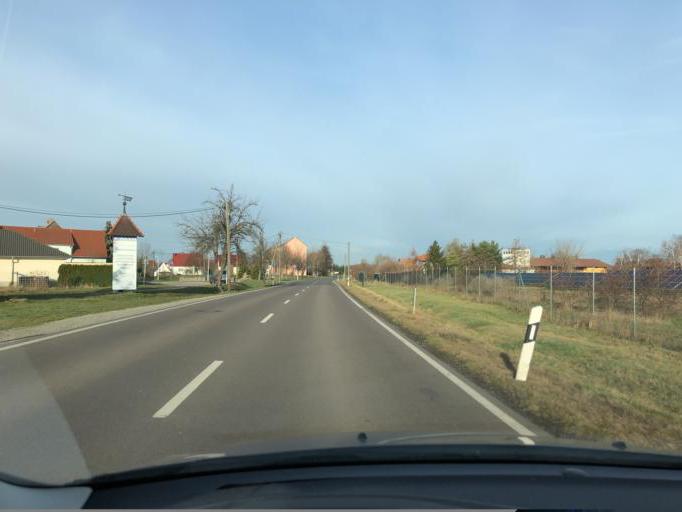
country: DE
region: Saxony-Anhalt
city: Reichardtswerben
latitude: 51.2500
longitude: 11.9625
